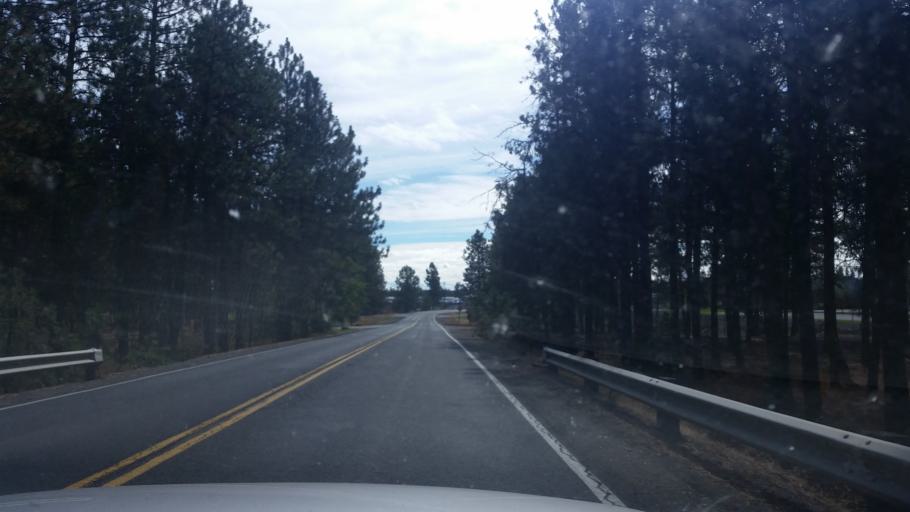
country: US
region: Washington
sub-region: Spokane County
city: Spokane
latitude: 47.6178
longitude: -117.4999
